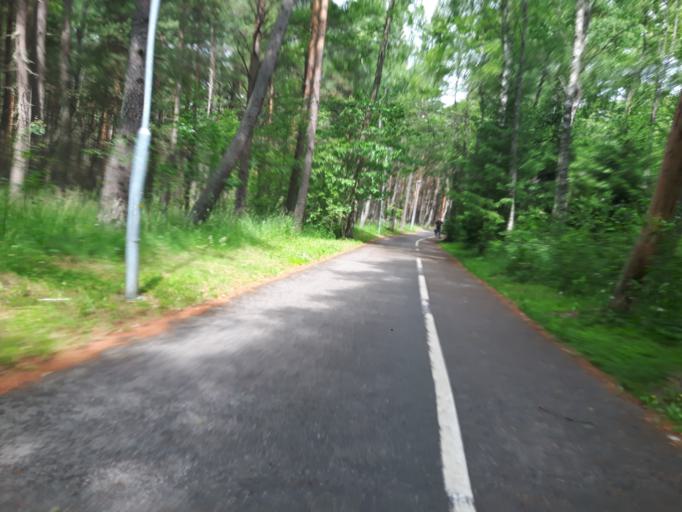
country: LT
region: Klaipedos apskritis
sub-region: Klaipeda
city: Klaipeda
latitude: 55.7550
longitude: 21.1146
